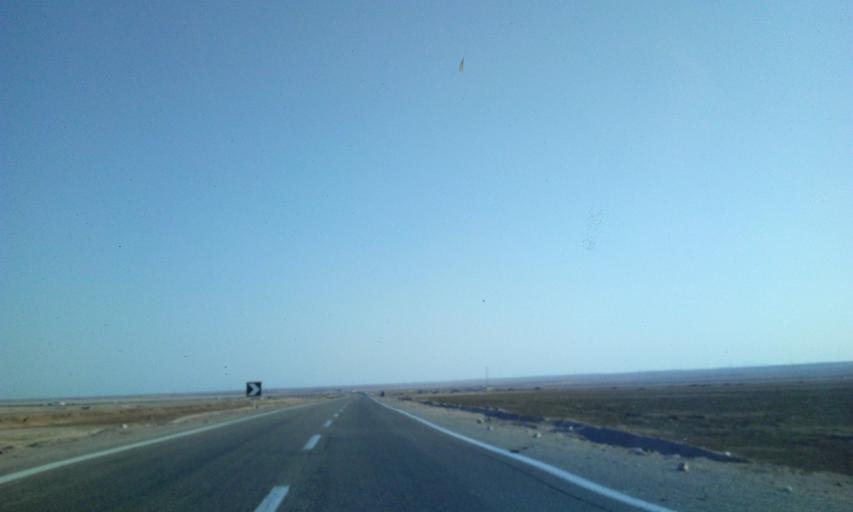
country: EG
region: South Sinai
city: Tor
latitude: 28.5907
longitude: 32.8635
